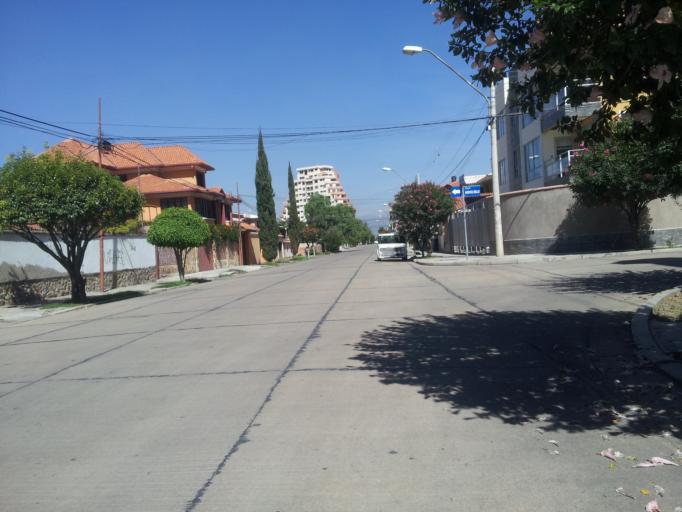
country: BO
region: Cochabamba
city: Cochabamba
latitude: -17.3810
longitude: -66.1719
